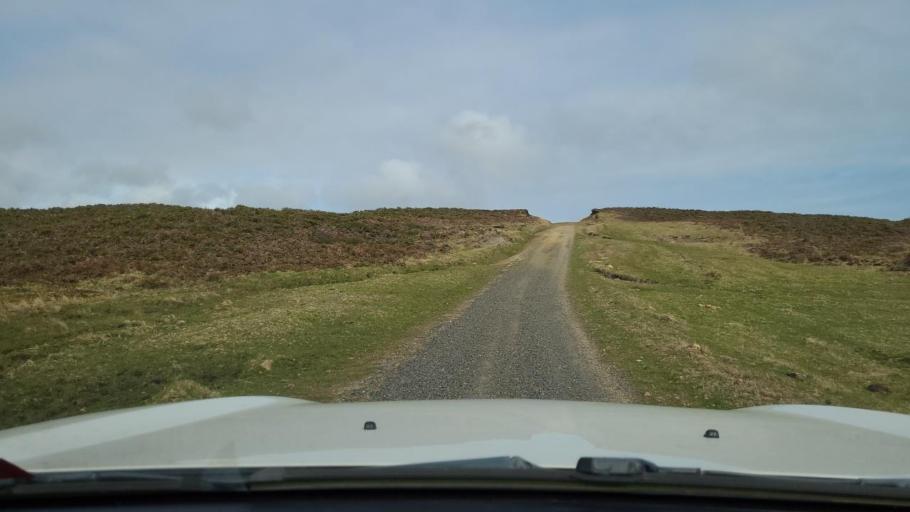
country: NZ
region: Chatham Islands
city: Waitangi
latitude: -44.0515
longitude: -176.6330
